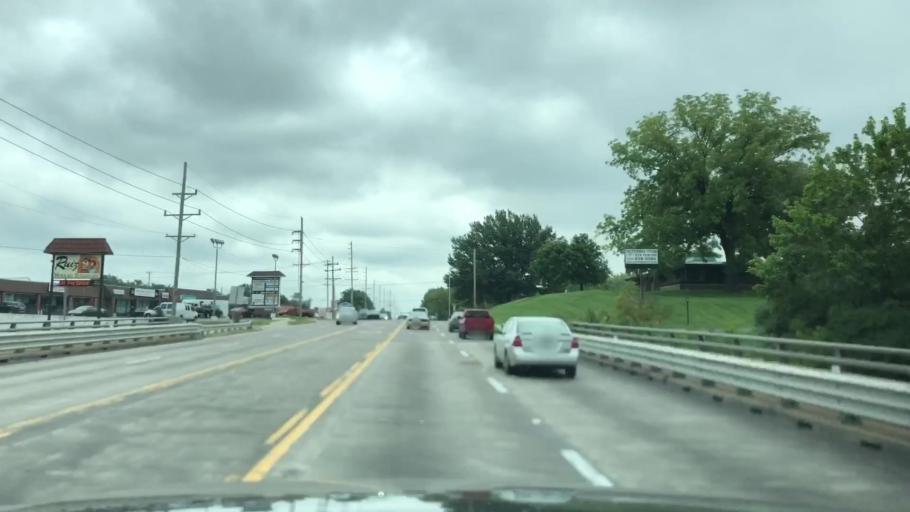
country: US
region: Missouri
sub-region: Saint Louis County
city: Florissant
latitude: 38.7999
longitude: -90.3318
